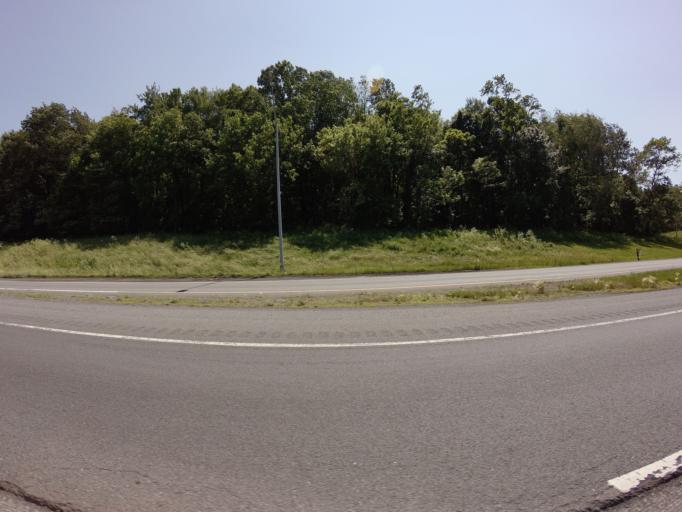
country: US
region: Maryland
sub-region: Frederick County
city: Linganore
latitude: 39.3761
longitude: -77.2351
